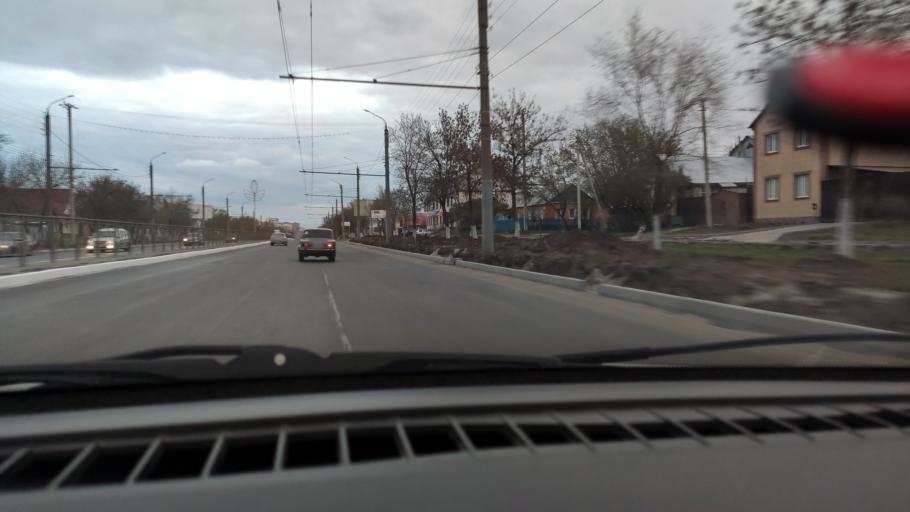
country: RU
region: Orenburg
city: Orenburg
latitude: 51.7898
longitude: 55.1068
